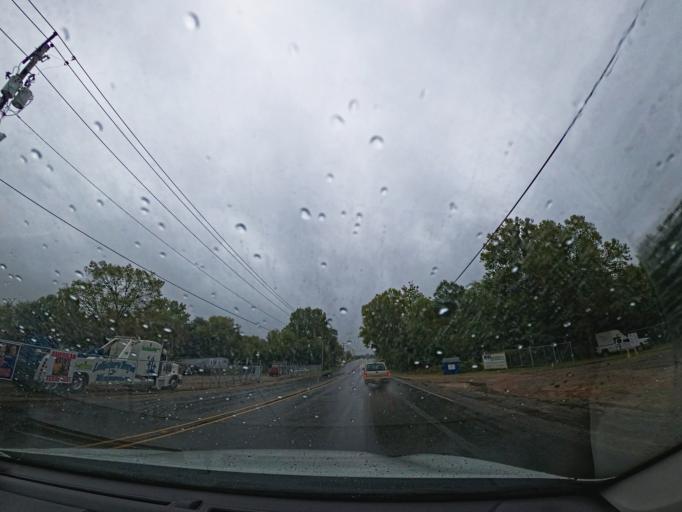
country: US
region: Texas
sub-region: Panola County
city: Carthage
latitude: 32.1579
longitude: -94.3312
